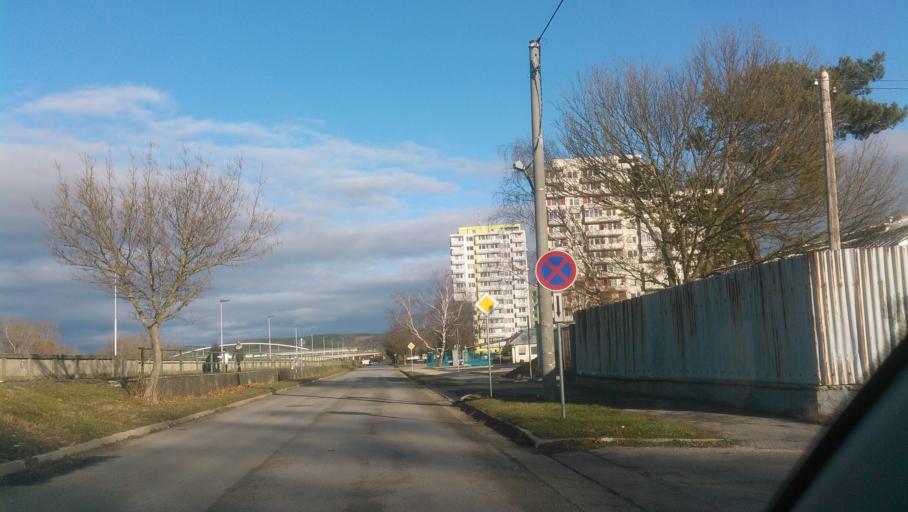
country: SK
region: Trnavsky
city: Hlohovec
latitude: 48.4257
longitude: 17.7883
